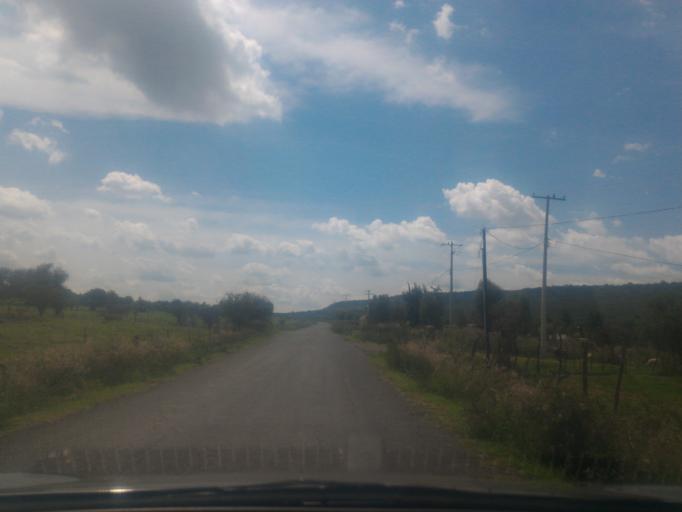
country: MX
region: Guanajuato
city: Ciudad Manuel Doblado
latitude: 20.8425
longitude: -102.0490
